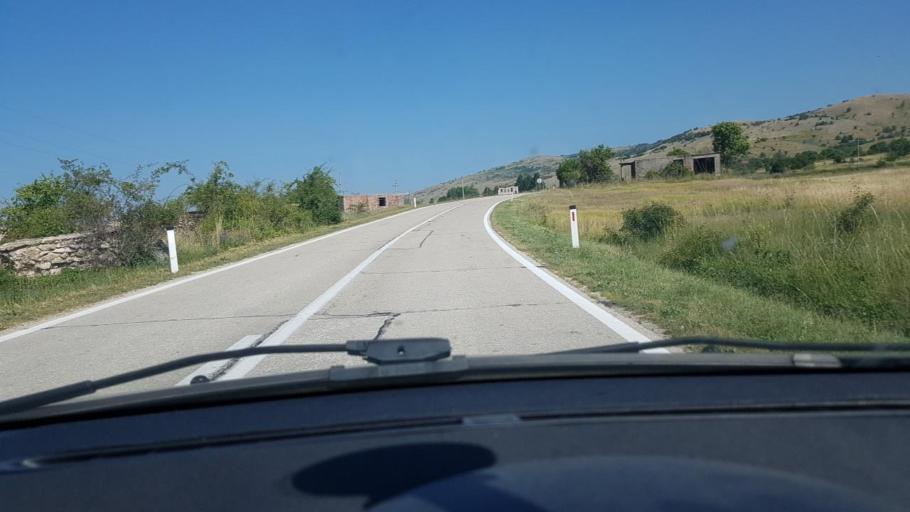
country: BA
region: Federation of Bosnia and Herzegovina
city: Bosansko Grahovo
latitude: 44.1153
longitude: 16.5382
